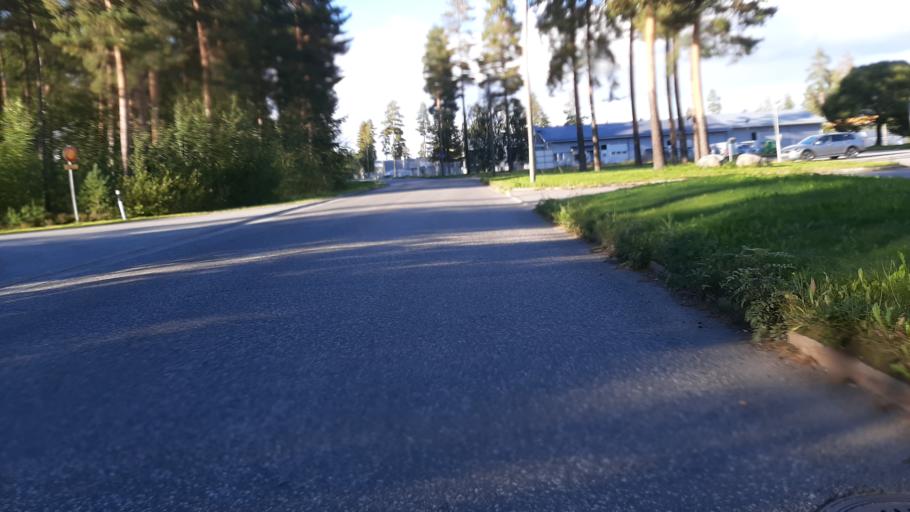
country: FI
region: North Karelia
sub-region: Joensuu
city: Joensuu
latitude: 62.6250
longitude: 29.7709
